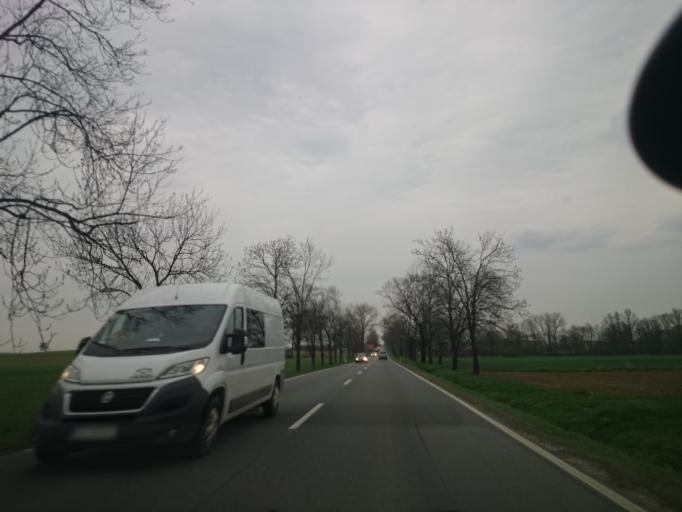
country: PL
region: Opole Voivodeship
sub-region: Powiat nyski
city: Pakoslawice
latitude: 50.5231
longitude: 17.3579
